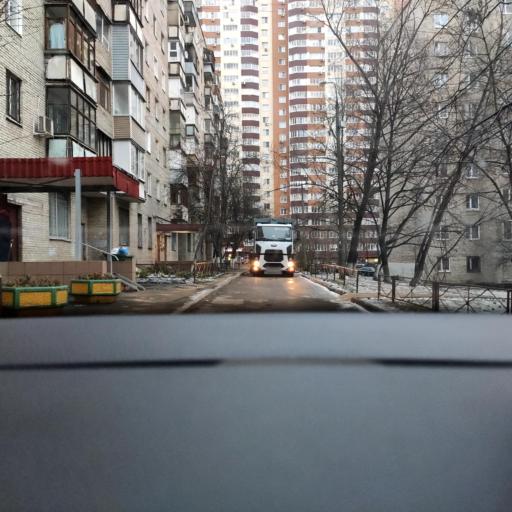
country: RU
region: Moskovskaya
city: Reutov
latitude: 55.7501
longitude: 37.8692
